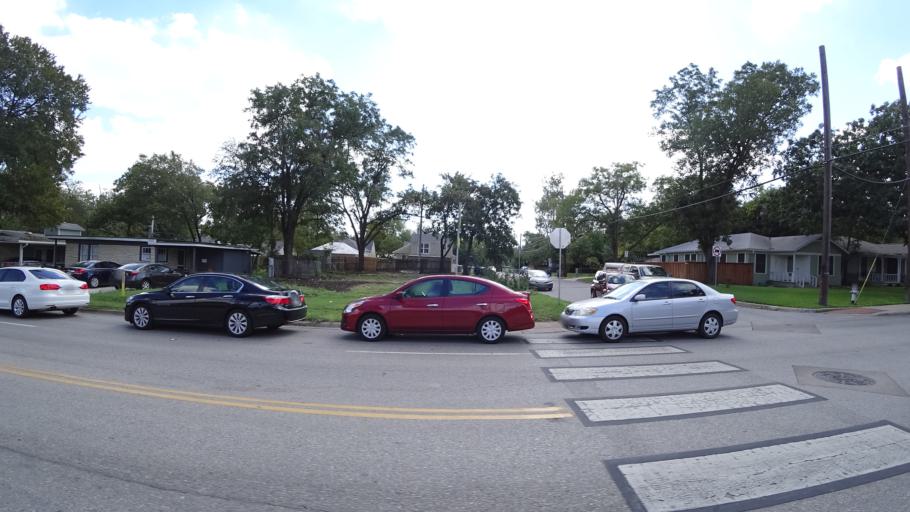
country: US
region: Texas
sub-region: Travis County
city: Austin
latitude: 30.3039
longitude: -97.7176
